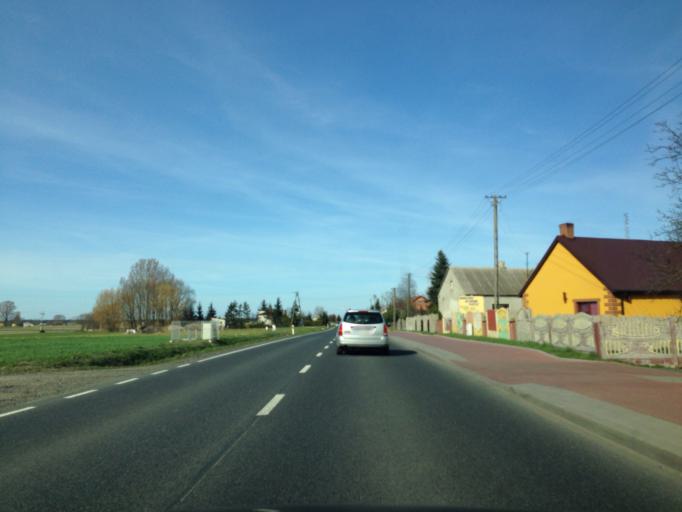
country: PL
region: Lodz Voivodeship
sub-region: Powiat poddebicki
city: Wartkowice
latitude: 51.9798
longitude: 19.0267
